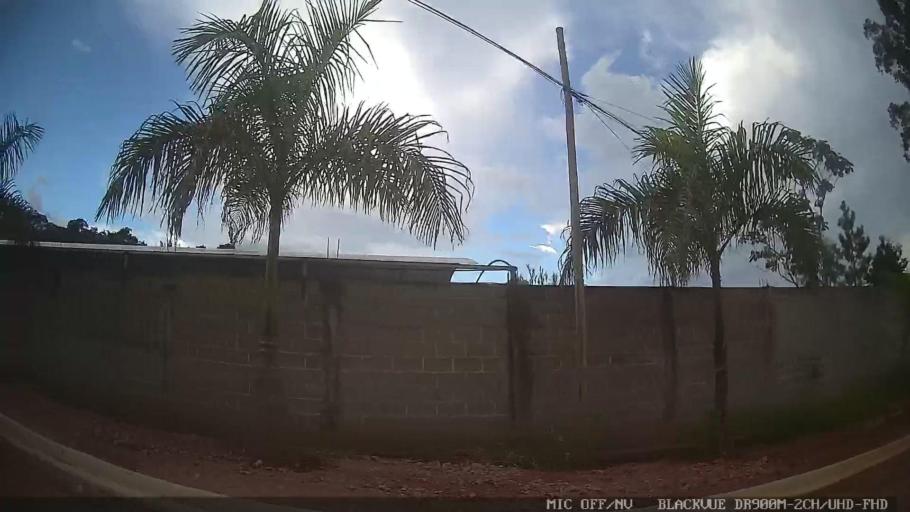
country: BR
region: Sao Paulo
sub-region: Bom Jesus Dos Perdoes
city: Bom Jesus dos Perdoes
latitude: -23.1112
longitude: -46.5024
